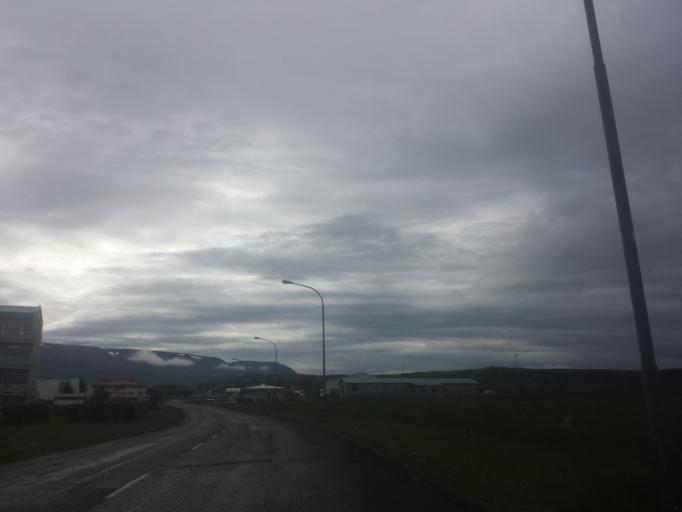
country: IS
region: Northwest
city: Saudarkrokur
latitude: 65.6574
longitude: -20.2906
